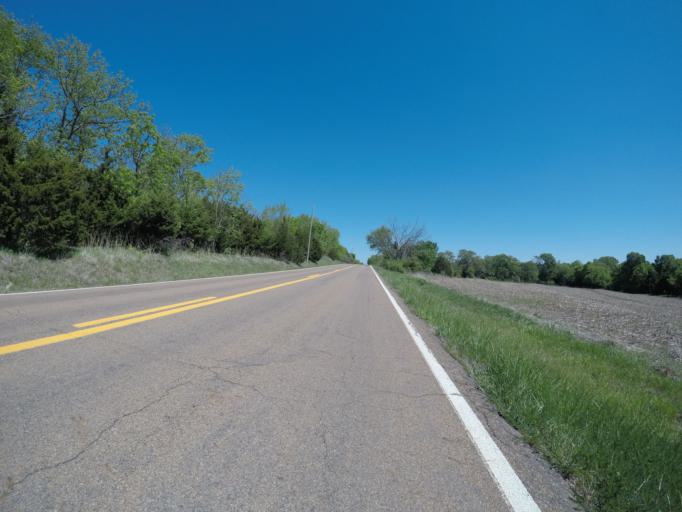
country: US
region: Kansas
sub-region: Osage County
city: Overbrook
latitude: 38.9224
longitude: -95.5192
